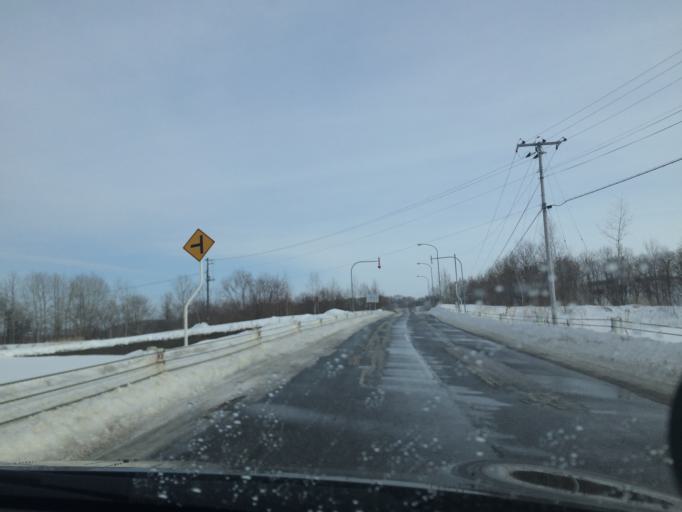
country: JP
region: Hokkaido
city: Obihiro
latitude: 42.9031
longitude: 143.0088
